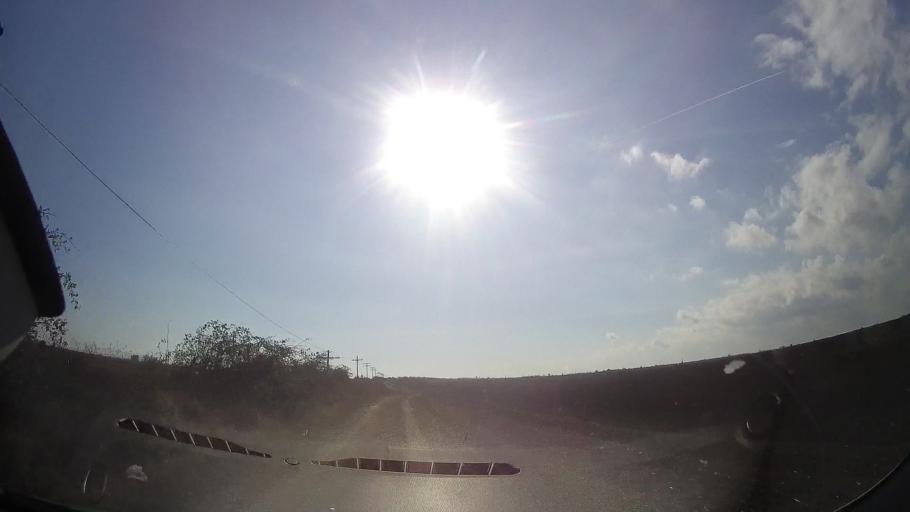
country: RO
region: Constanta
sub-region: Comuna Tuzla
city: Tuzla
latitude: 43.9810
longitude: 28.6444
